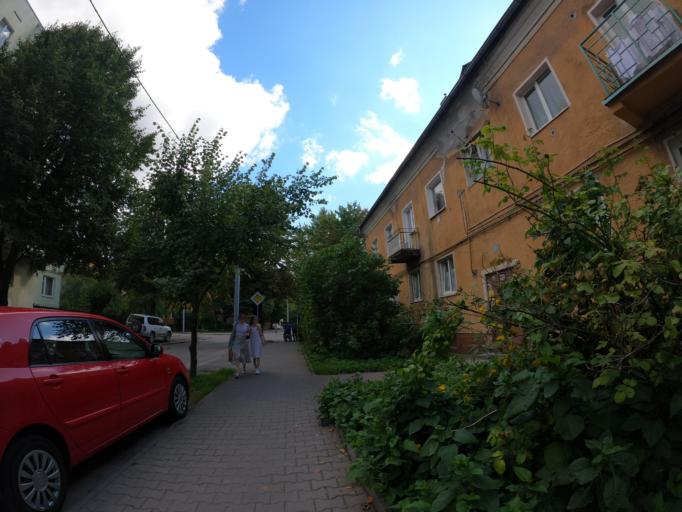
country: RU
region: Kaliningrad
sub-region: Gorod Kaliningrad
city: Kaliningrad
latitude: 54.7307
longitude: 20.4743
